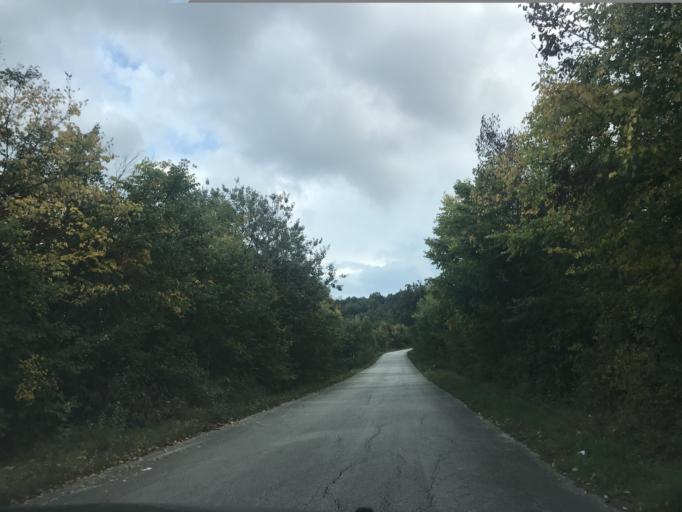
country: IT
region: Molise
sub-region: Provincia di Campobasso
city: Duronia
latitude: 41.6682
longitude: 14.4602
